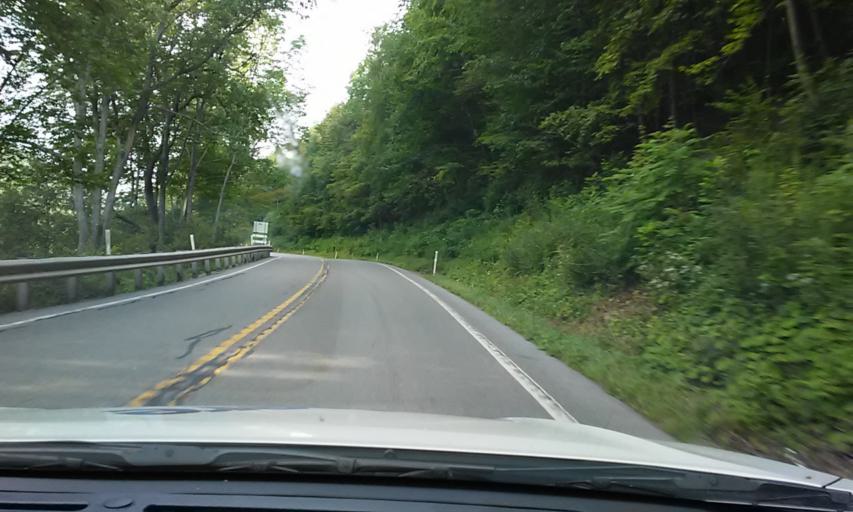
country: US
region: Pennsylvania
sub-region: Potter County
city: Galeton
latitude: 41.8233
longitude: -77.7973
